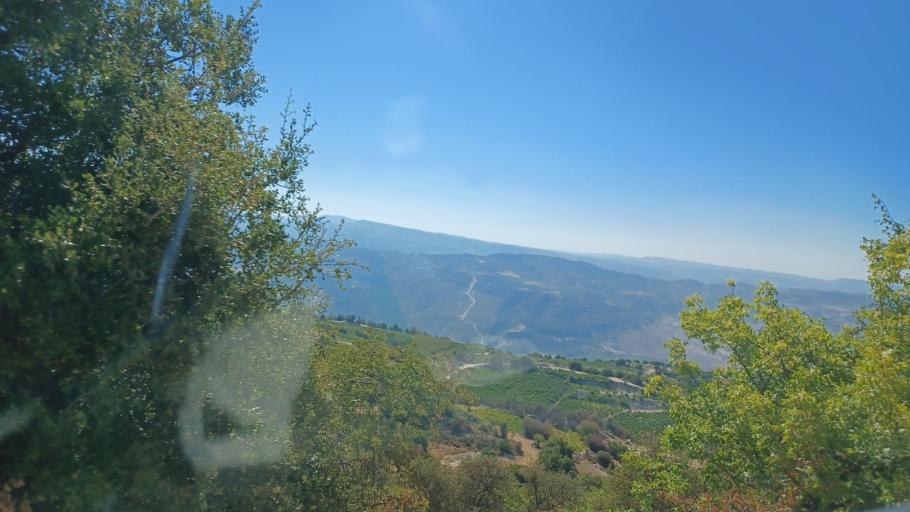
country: CY
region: Limassol
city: Pachna
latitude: 34.9057
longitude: 32.6375
